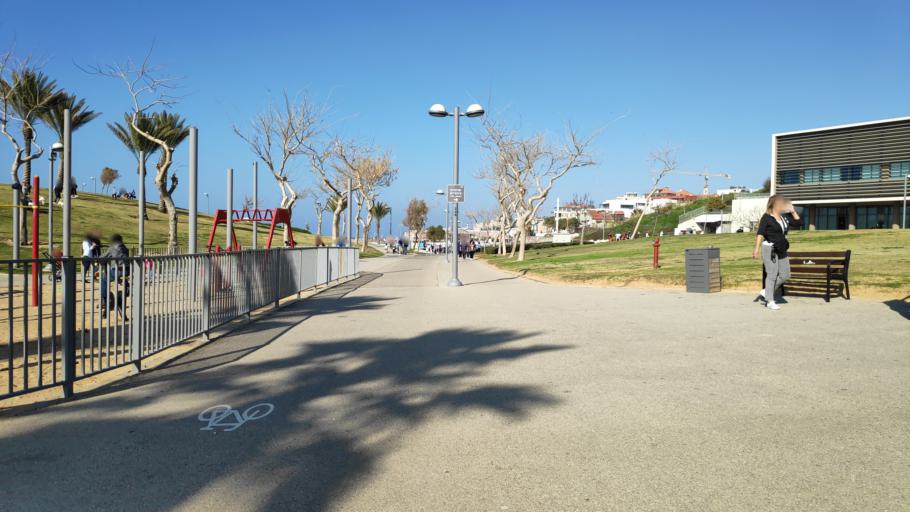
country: IL
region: Tel Aviv
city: Yafo
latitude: 32.0465
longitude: 34.7471
